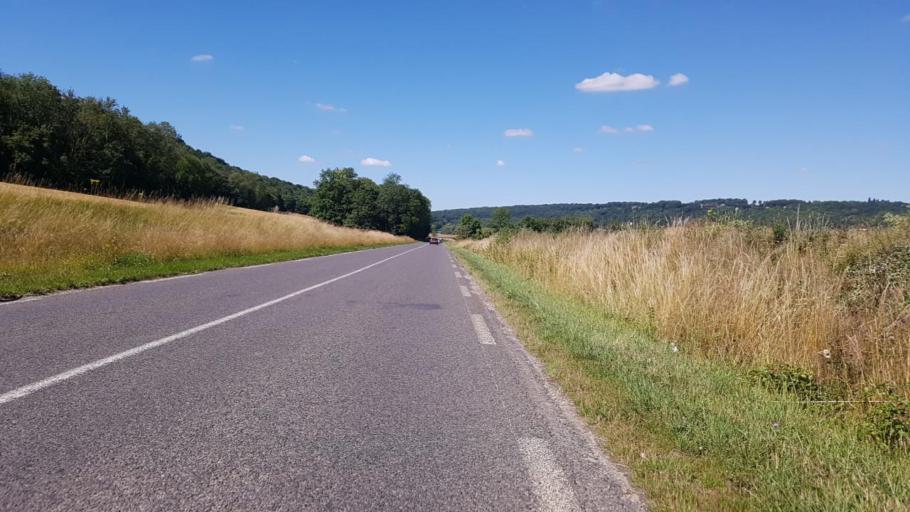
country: FR
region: Ile-de-France
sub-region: Departement de Seine-et-Marne
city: Chamigny
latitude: 48.9719
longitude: 3.1746
